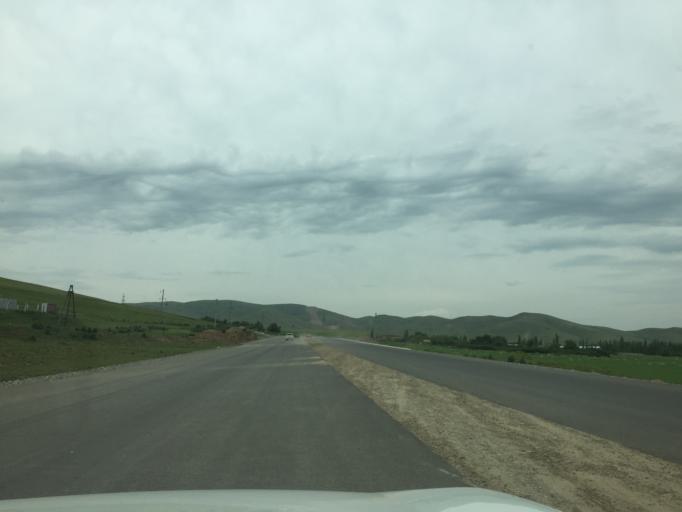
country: KZ
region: Ongtustik Qazaqstan
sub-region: Tulkibas Audany
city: Zhabagly
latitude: 42.5124
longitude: 70.5281
